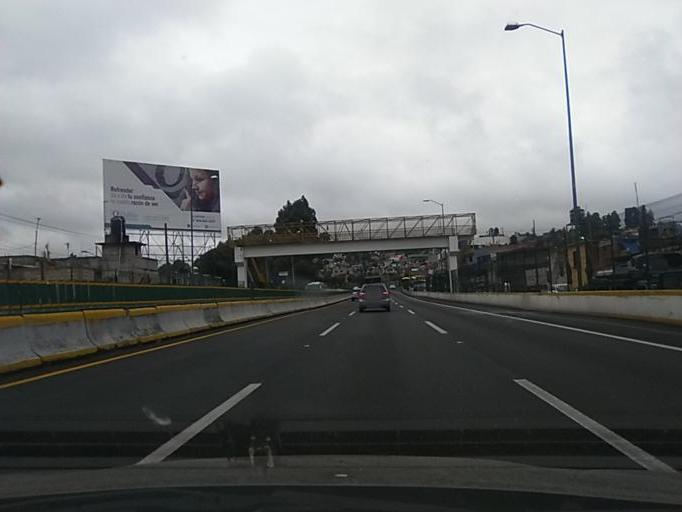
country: MX
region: Mexico City
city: Xochimilco
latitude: 19.1998
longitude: -99.1414
